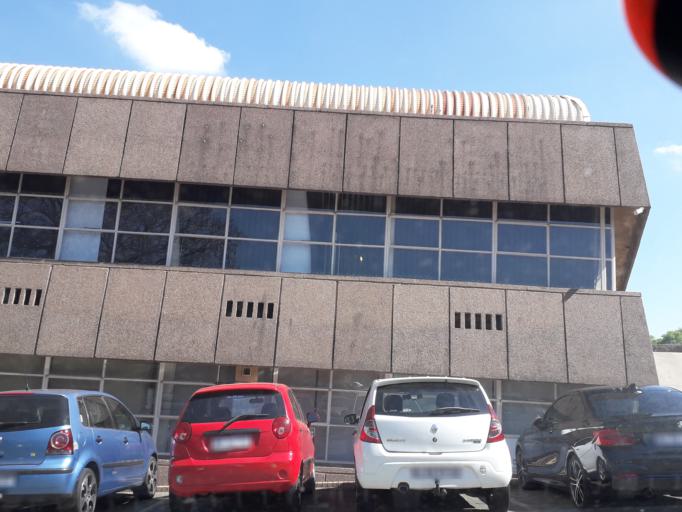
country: ZA
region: Gauteng
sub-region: City of Johannesburg Metropolitan Municipality
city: Modderfontein
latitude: -26.0900
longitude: 28.0770
